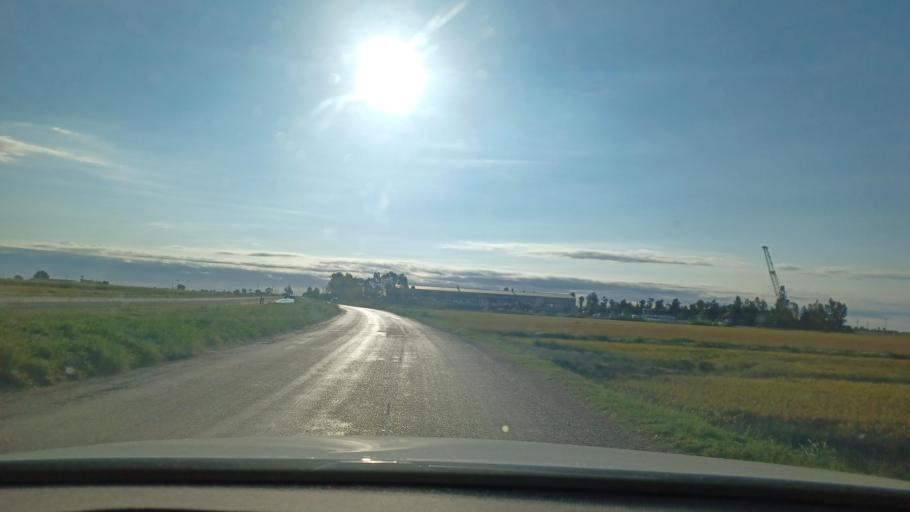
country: ES
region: Catalonia
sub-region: Provincia de Tarragona
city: Amposta
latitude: 40.7014
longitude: 0.5993
